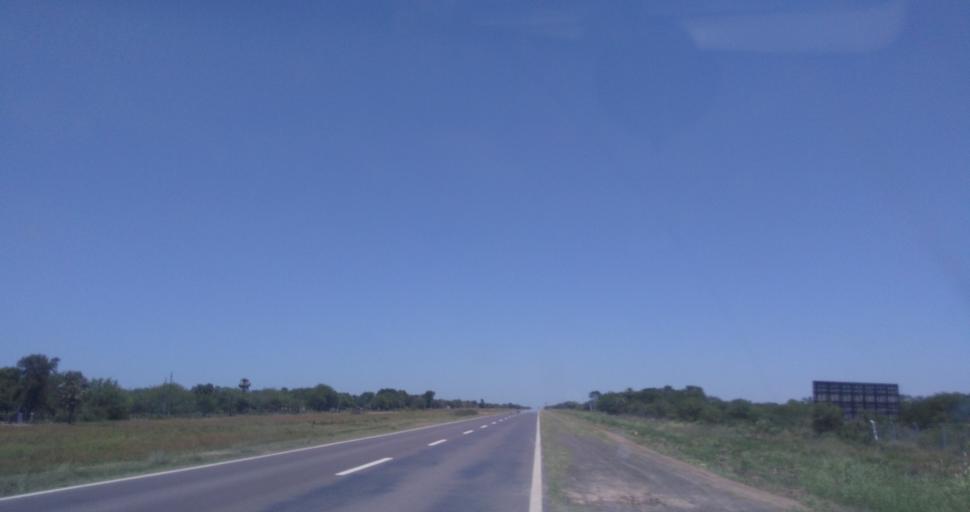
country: AR
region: Chaco
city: Fontana
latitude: -27.4769
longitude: -59.0580
